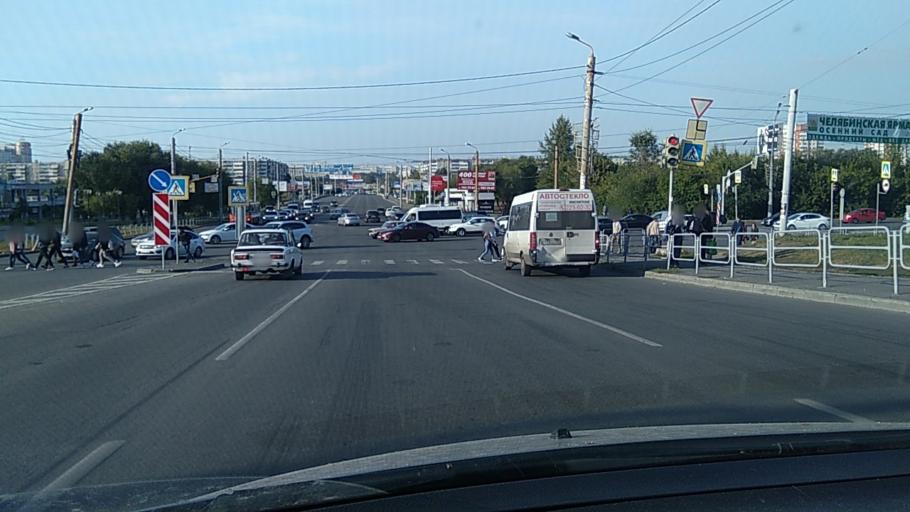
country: RU
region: Chelyabinsk
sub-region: Gorod Chelyabinsk
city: Chelyabinsk
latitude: 55.1703
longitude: 61.3583
